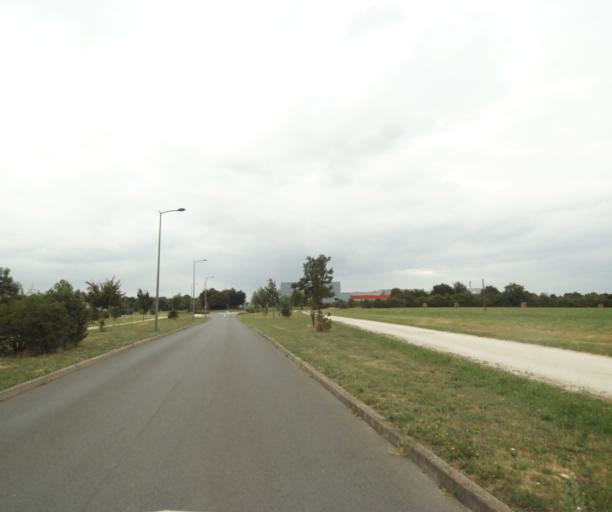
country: FR
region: Pays de la Loire
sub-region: Departement de la Sarthe
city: Sable-sur-Sarthe
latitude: 47.8260
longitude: -0.3213
